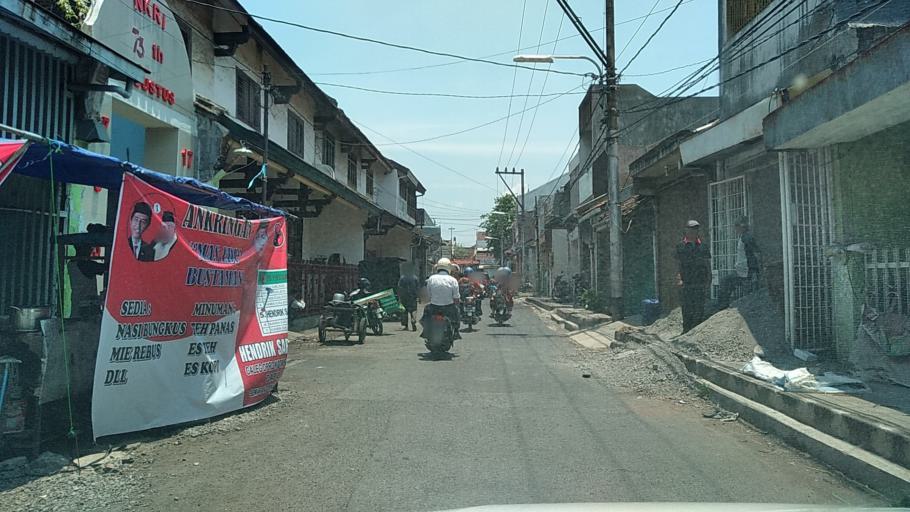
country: ID
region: Central Java
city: Semarang
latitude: -6.9745
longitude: 110.4301
